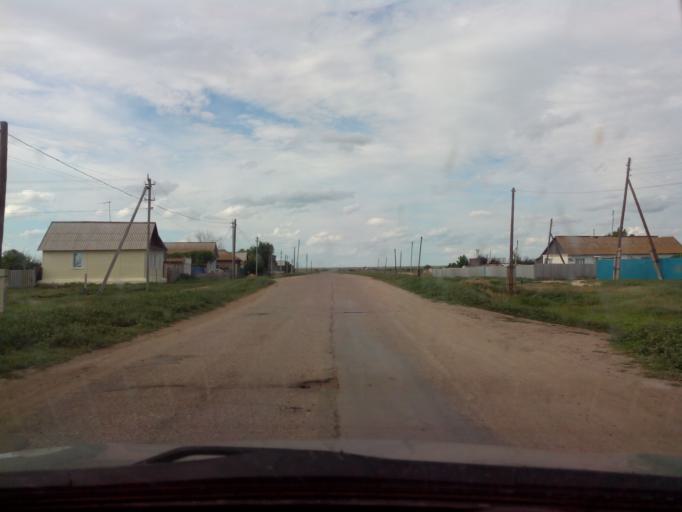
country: RU
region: Volgograd
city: Leninsk
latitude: 48.6685
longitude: 45.3681
